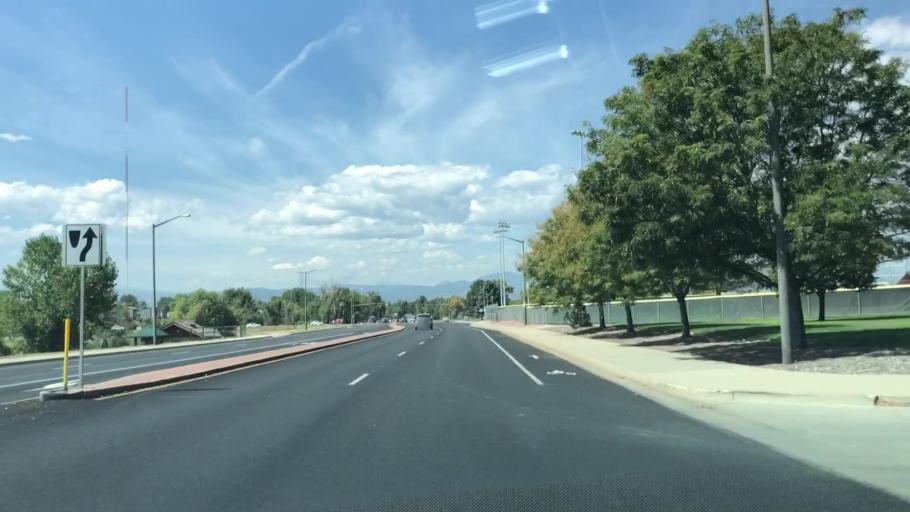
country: US
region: Colorado
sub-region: Larimer County
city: Loveland
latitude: 40.3928
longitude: -105.0935
